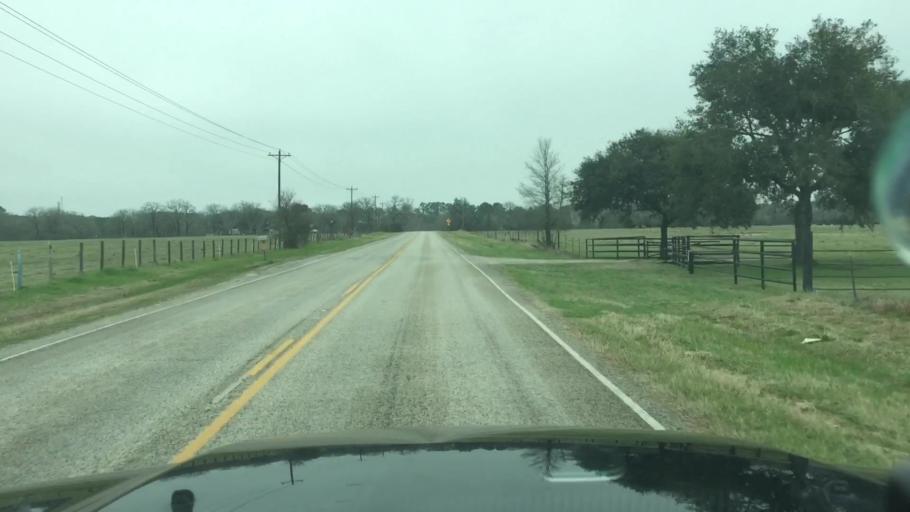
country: US
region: Texas
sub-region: Fayette County
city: La Grange
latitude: 30.0038
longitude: -96.9012
